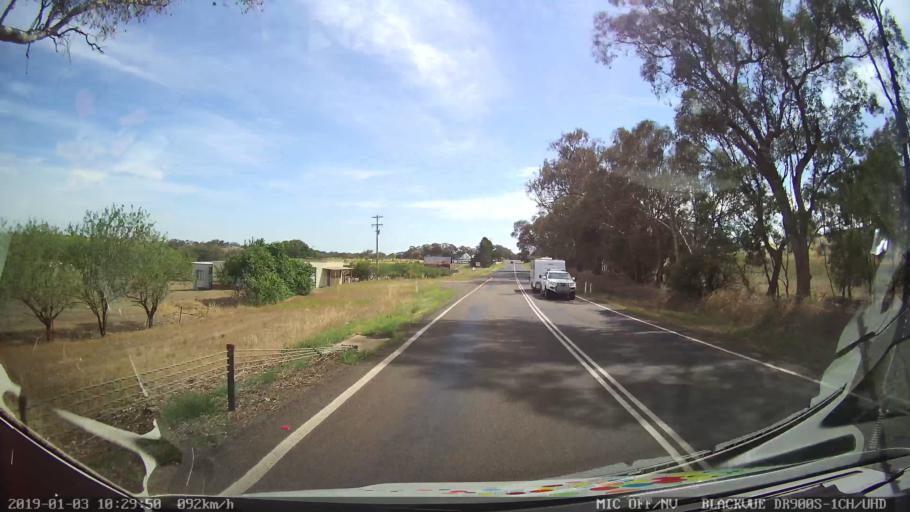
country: AU
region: New South Wales
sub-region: Young
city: Young
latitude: -34.3690
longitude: 148.2619
